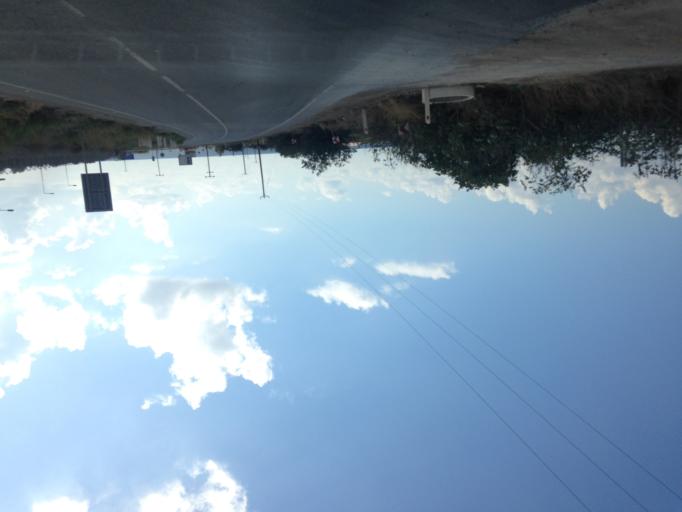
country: CY
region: Pafos
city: Paphos
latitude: 34.7134
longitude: 32.5122
